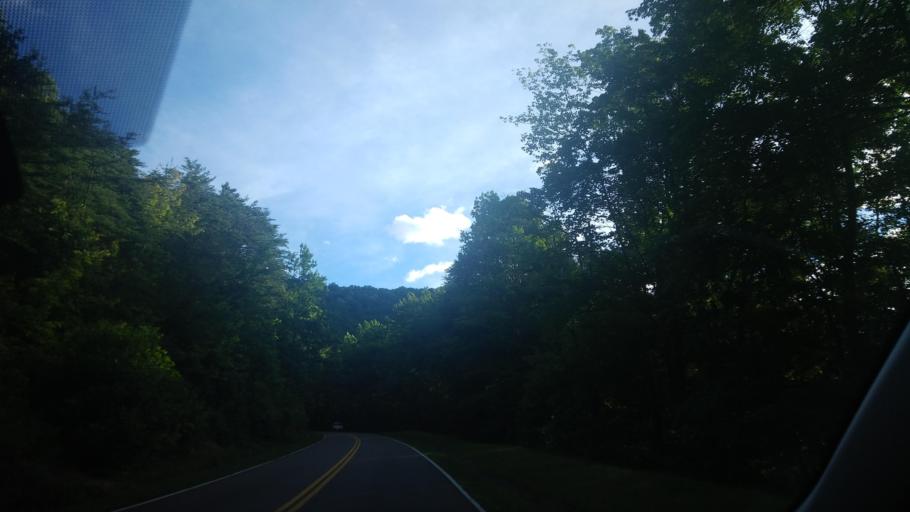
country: US
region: Tennessee
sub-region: Cocke County
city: Newport
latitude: 35.8050
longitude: -83.2385
